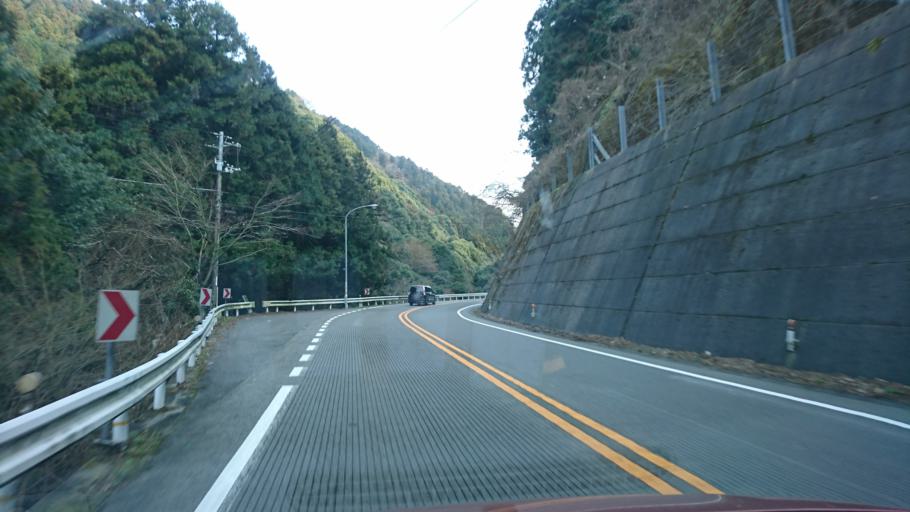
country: JP
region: Ehime
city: Hojo
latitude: 33.9643
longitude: 132.9060
